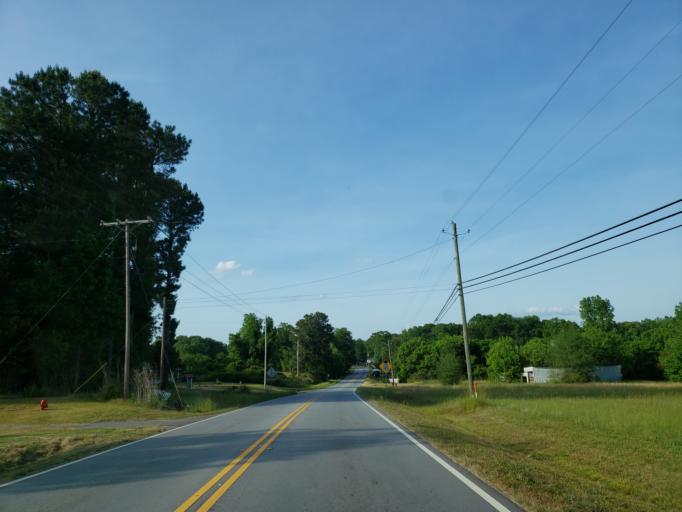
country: US
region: Georgia
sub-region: Carroll County
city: Bowdon
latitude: 33.5229
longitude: -85.2577
